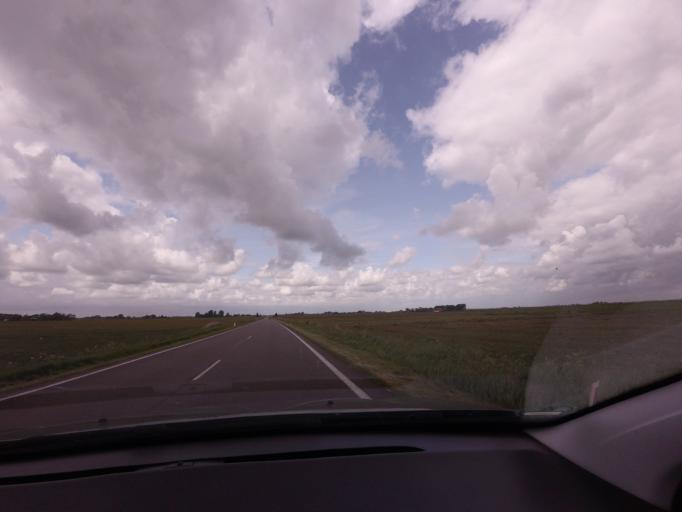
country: NL
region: Friesland
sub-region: Sudwest Fryslan
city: Workum
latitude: 52.9847
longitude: 5.4633
